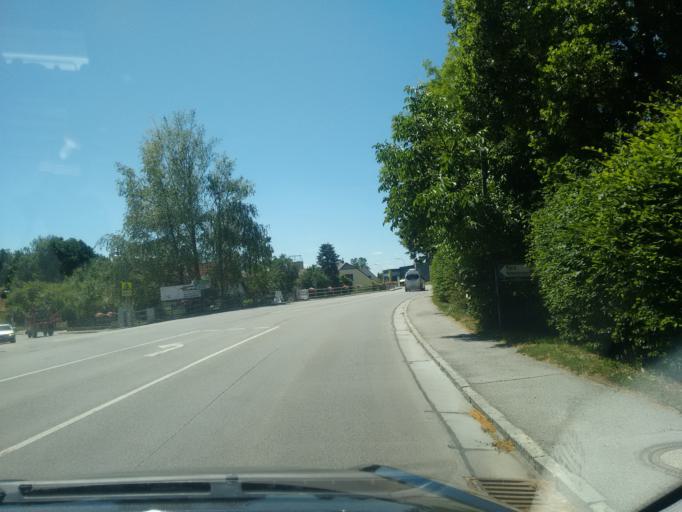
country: AT
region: Lower Austria
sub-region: Politischer Bezirk Sankt Polten
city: Herzogenburg
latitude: 48.2383
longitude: 15.6971
